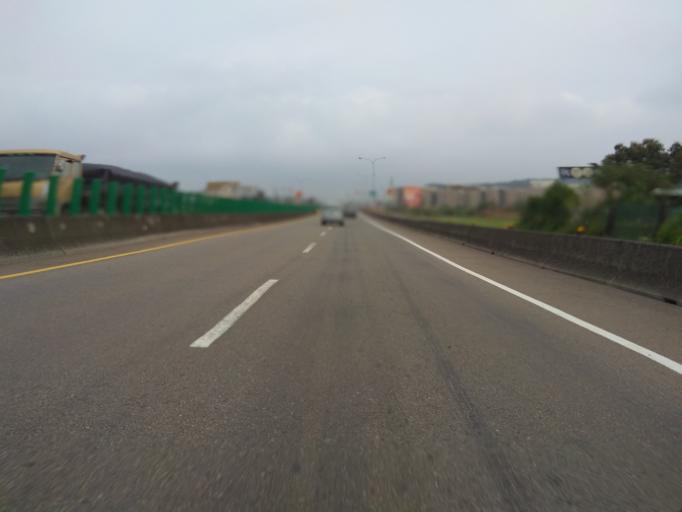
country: TW
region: Taiwan
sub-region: Hsinchu
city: Zhubei
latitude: 24.8696
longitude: 120.9535
